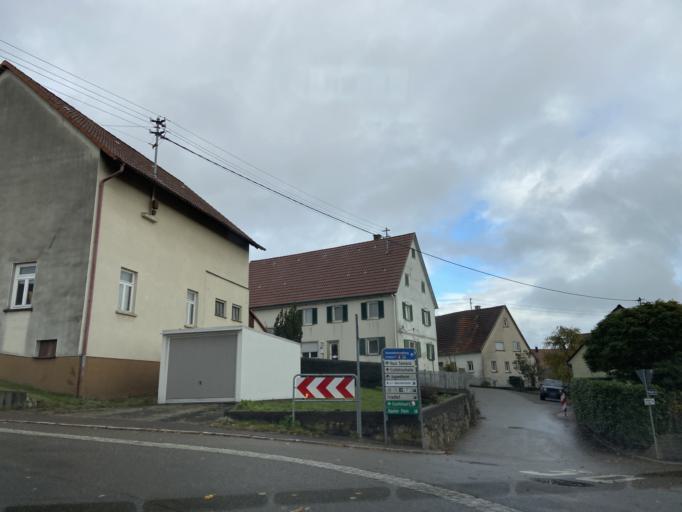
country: DE
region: Baden-Wuerttemberg
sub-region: Freiburg Region
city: Irndorf
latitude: 48.0666
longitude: 8.9732
